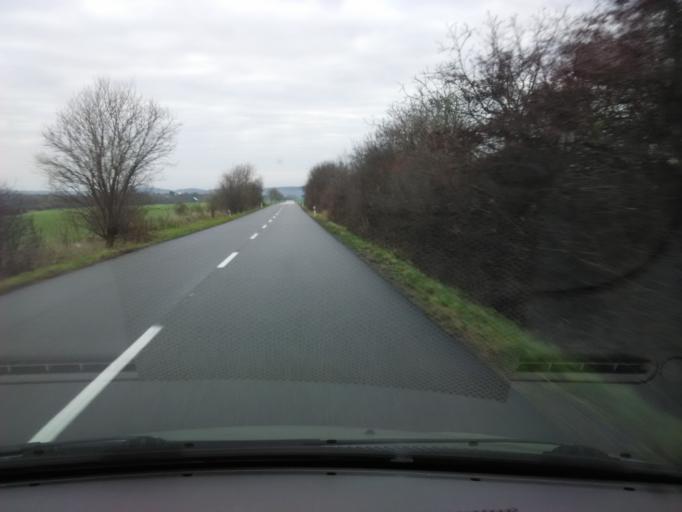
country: SK
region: Nitriansky
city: Tlmace
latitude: 48.3358
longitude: 18.4907
